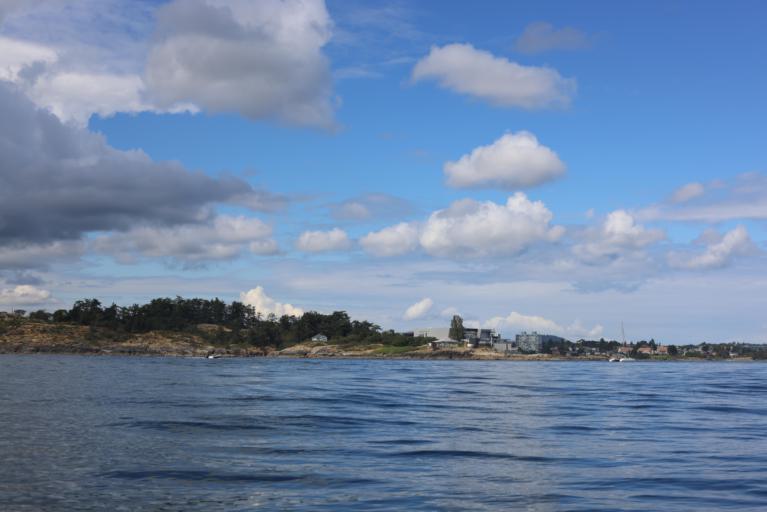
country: CA
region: British Columbia
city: Victoria
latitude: 48.4137
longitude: -123.4011
